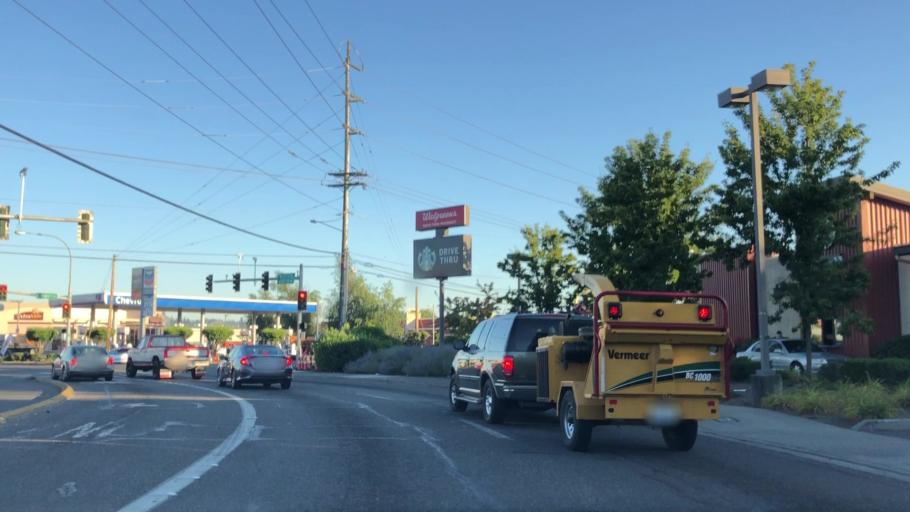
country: US
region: Washington
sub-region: King County
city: Auburn
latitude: 47.3208
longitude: -122.2208
